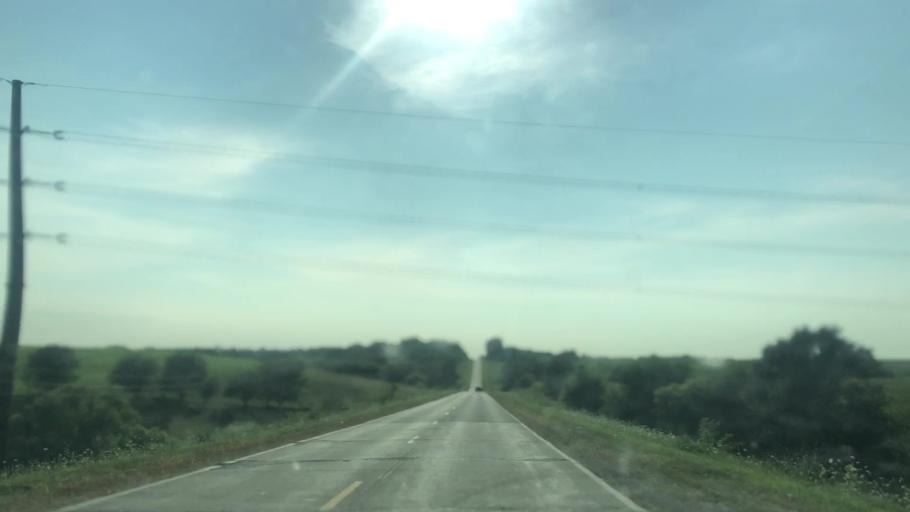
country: US
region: Iowa
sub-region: Marshall County
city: Marshalltown
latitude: 42.0488
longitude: -92.9652
